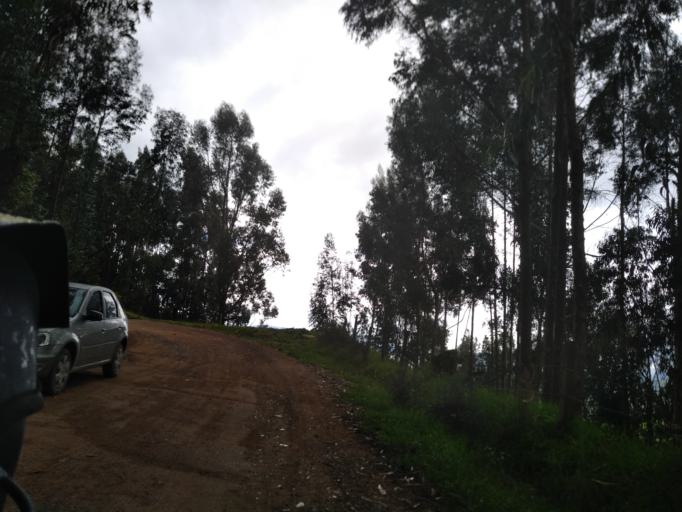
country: CO
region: Boyaca
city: Sotaquira
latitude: 5.7662
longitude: -73.2703
